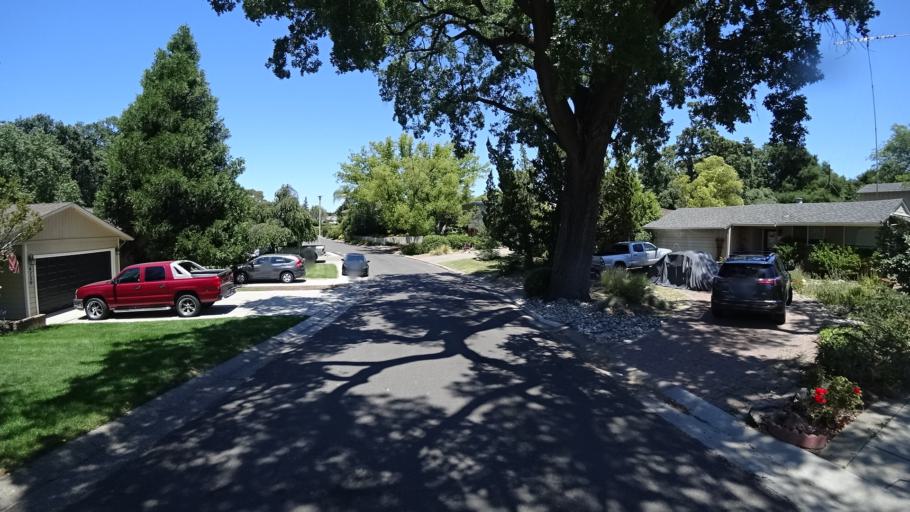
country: US
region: California
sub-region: Sacramento County
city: Sacramento
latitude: 38.5354
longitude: -121.5063
